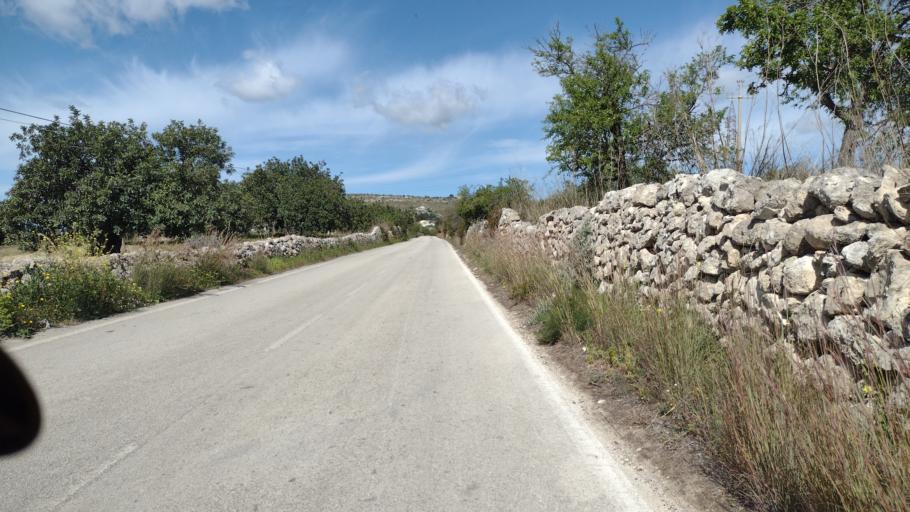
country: IT
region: Sicily
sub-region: Provincia di Siracusa
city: Noto
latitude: 36.9029
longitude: 15.0383
